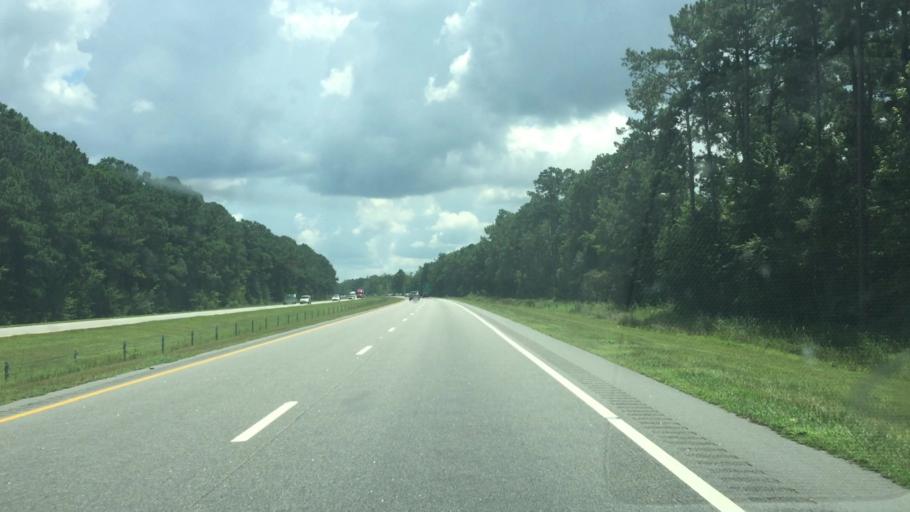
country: US
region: North Carolina
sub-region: Columbus County
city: Chadbourn
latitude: 34.4061
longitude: -78.9238
